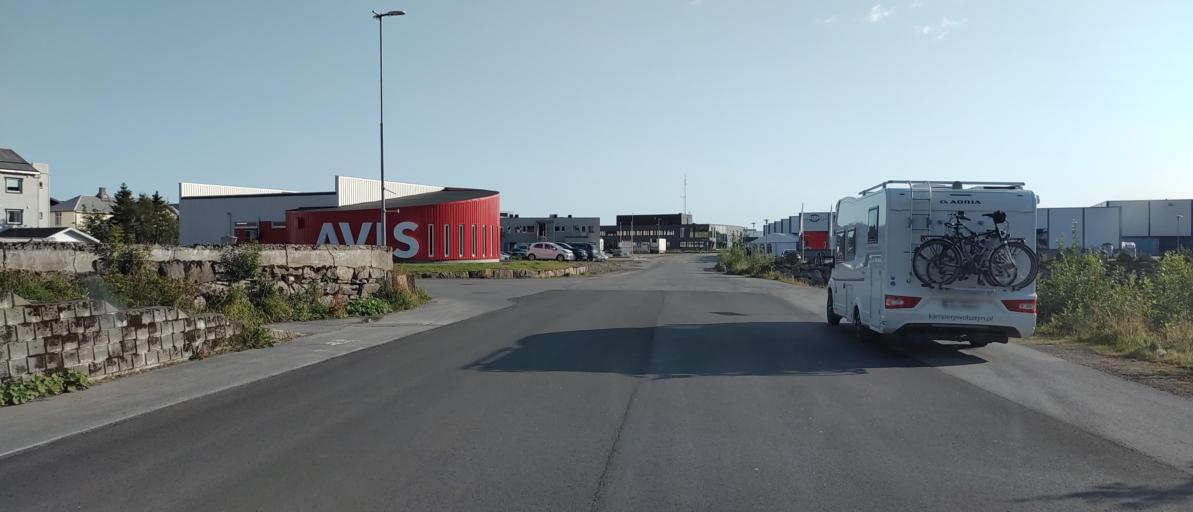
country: NO
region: Nordland
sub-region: Vagan
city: Svolvaer
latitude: 68.2315
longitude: 14.5593
